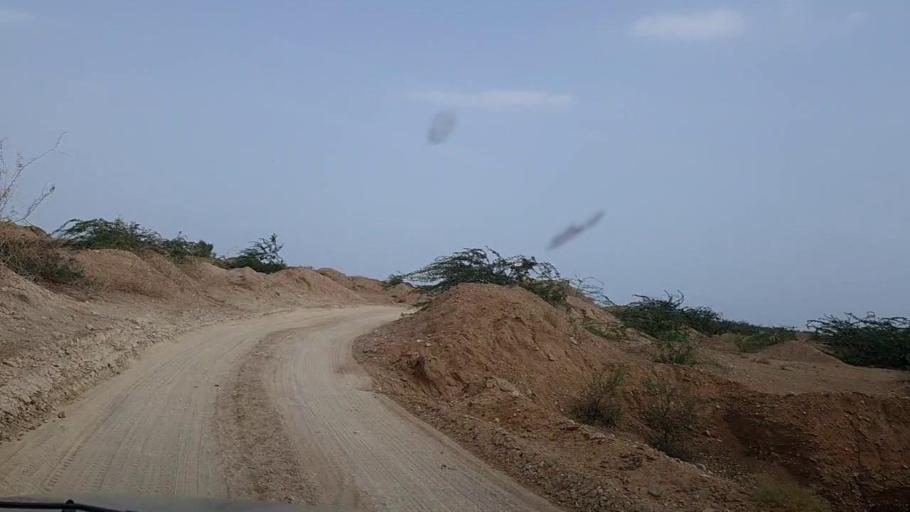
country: PK
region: Sindh
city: Kotri
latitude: 25.2802
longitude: 68.2682
